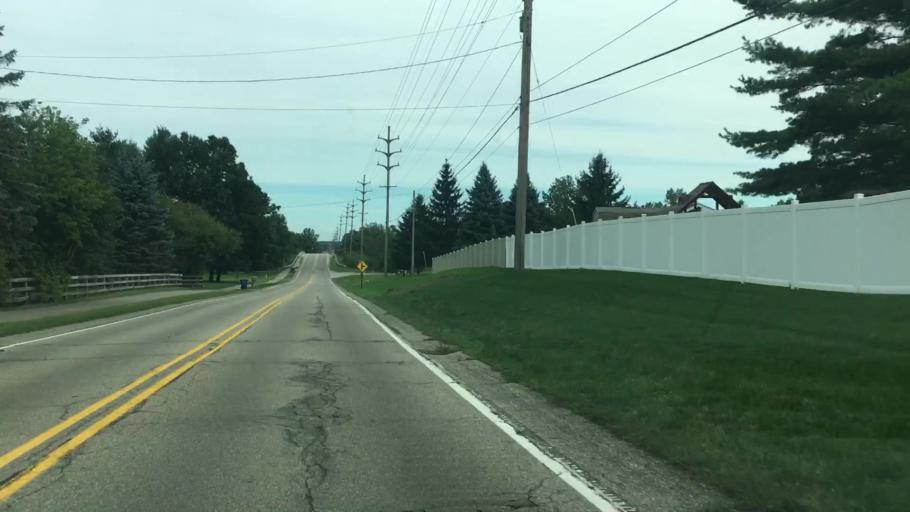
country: US
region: Michigan
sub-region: Ottawa County
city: Jenison
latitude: 42.8737
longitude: -85.7823
